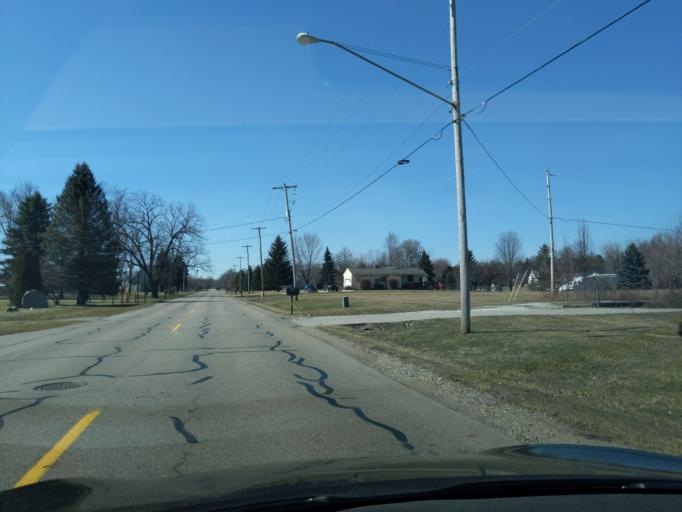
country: US
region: Michigan
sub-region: Eaton County
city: Grand Ledge
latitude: 42.7266
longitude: -84.6873
